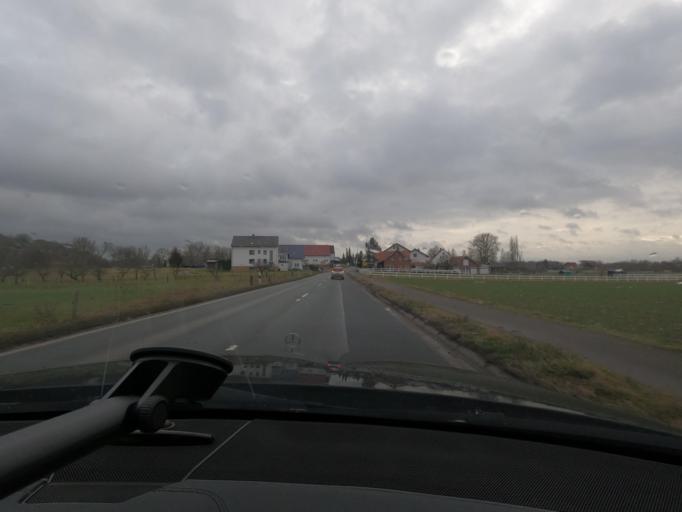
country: DE
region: Hesse
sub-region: Regierungsbezirk Kassel
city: Volkmarsen
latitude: 51.4196
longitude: 9.1232
